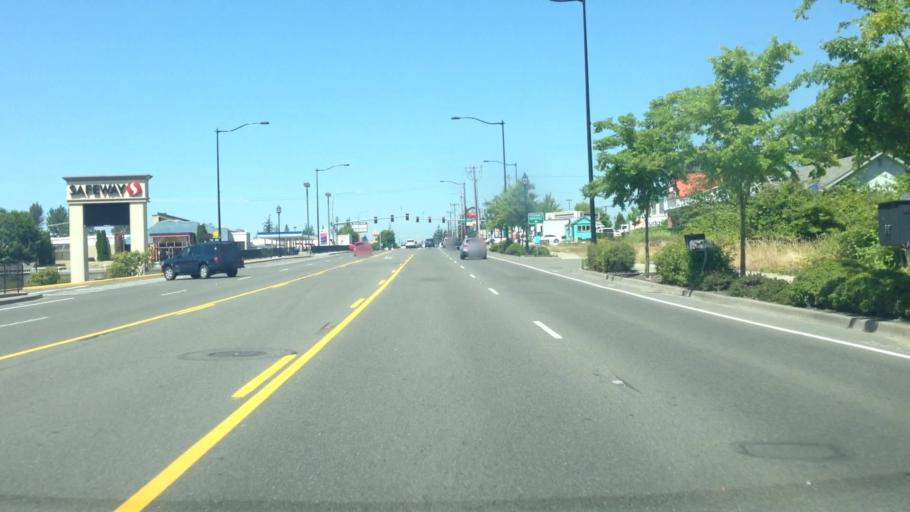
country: US
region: Washington
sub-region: Pierce County
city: Edgewood
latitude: 47.2482
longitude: -122.2938
